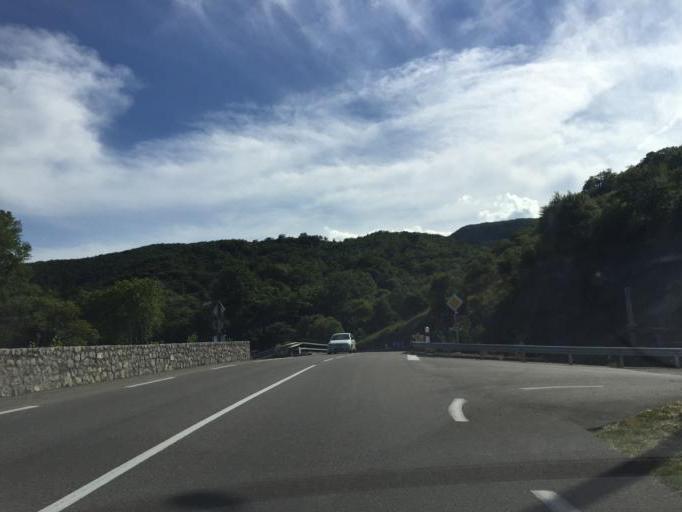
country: FR
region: Rhone-Alpes
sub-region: Departement de la Drome
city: Saulce-sur-Rhone
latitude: 44.7085
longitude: 4.7656
